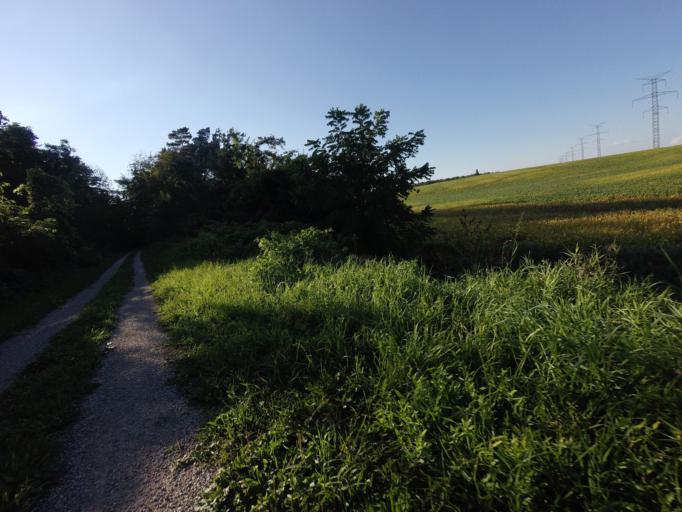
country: CA
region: Ontario
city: Goderich
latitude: 43.7499
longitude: -81.6561
